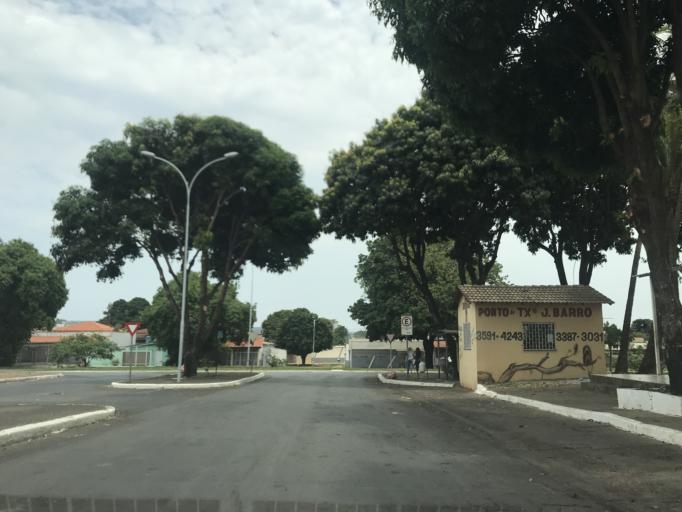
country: BR
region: Federal District
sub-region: Brasilia
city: Brasilia
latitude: -15.6453
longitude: -47.8024
